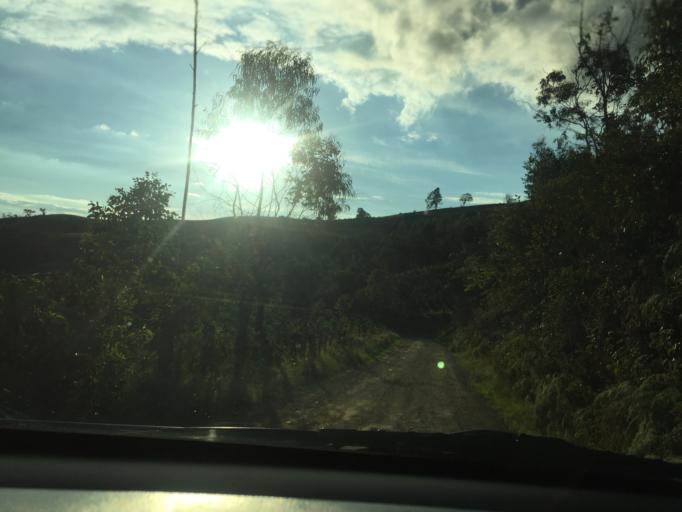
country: CO
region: Cundinamarca
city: Zipacon
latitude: 4.7322
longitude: -74.3888
